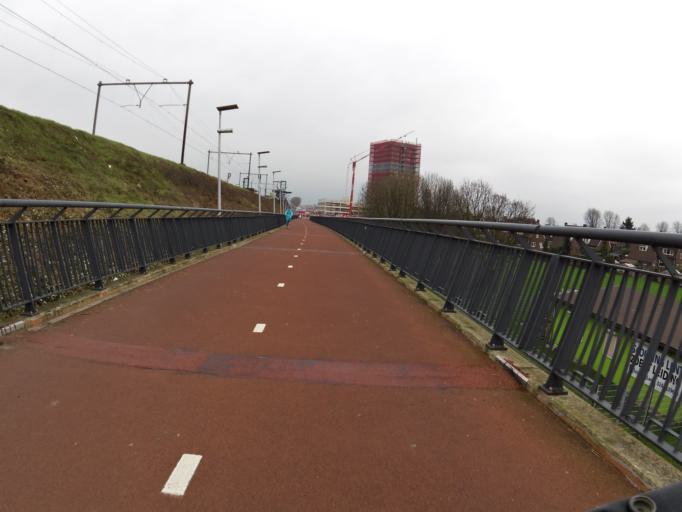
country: NL
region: Gelderland
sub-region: Gemeente Nijmegen
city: Nijmegen
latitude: 51.8601
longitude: 5.8601
